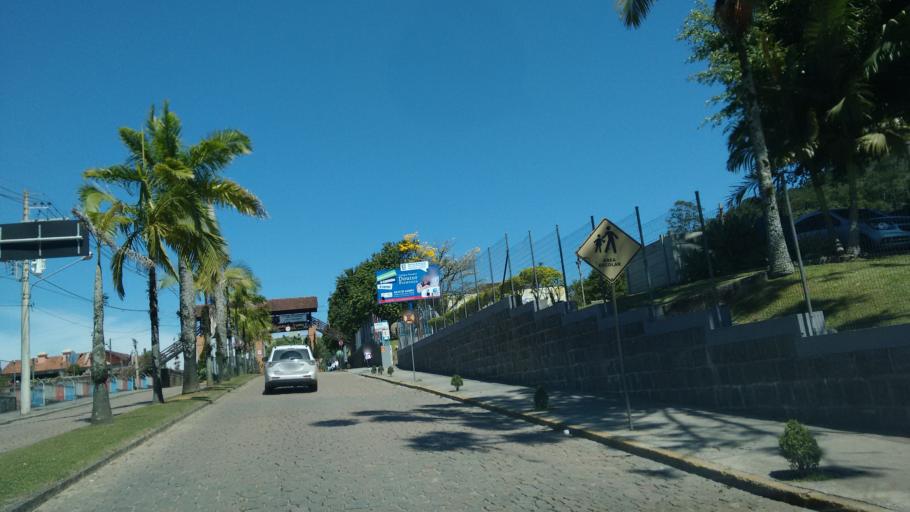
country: BR
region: Santa Catarina
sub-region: Pomerode
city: Pomerode
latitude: -26.7379
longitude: -49.1784
